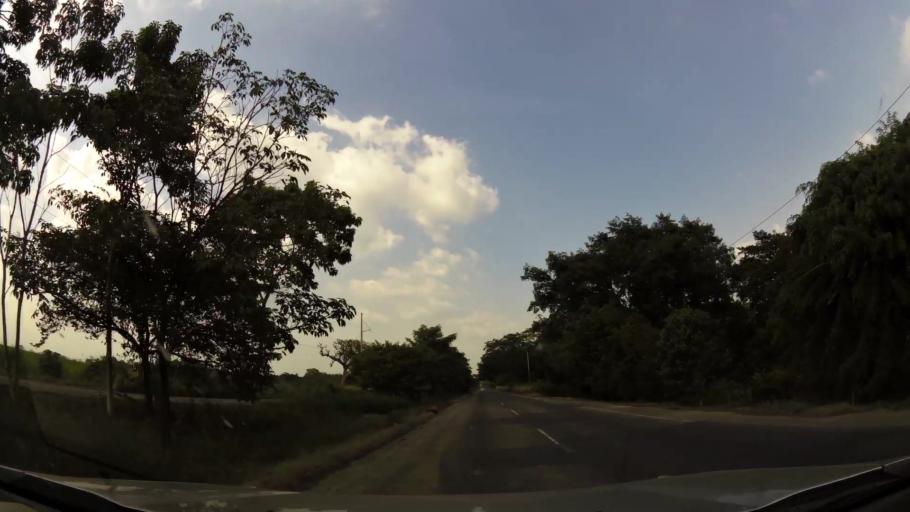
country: GT
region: Escuintla
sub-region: Municipio de Masagua
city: Masagua
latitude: 14.0735
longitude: -90.7773
